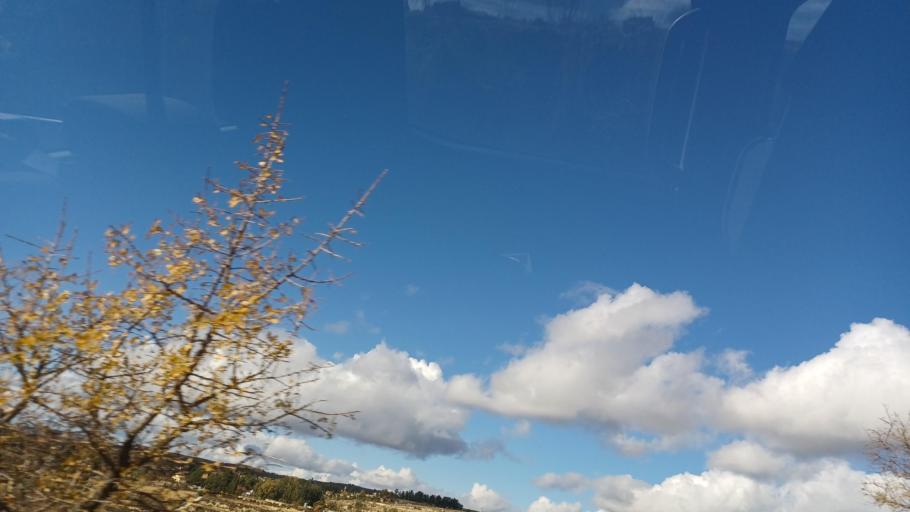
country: CY
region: Limassol
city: Pachna
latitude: 34.8156
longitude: 32.7936
